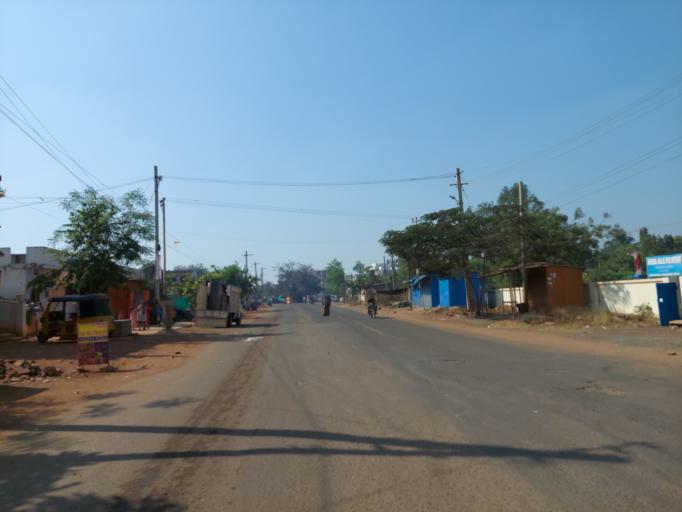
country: IN
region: Telangana
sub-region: Rangareddi
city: Vikarabad
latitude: 17.3391
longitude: 77.8973
